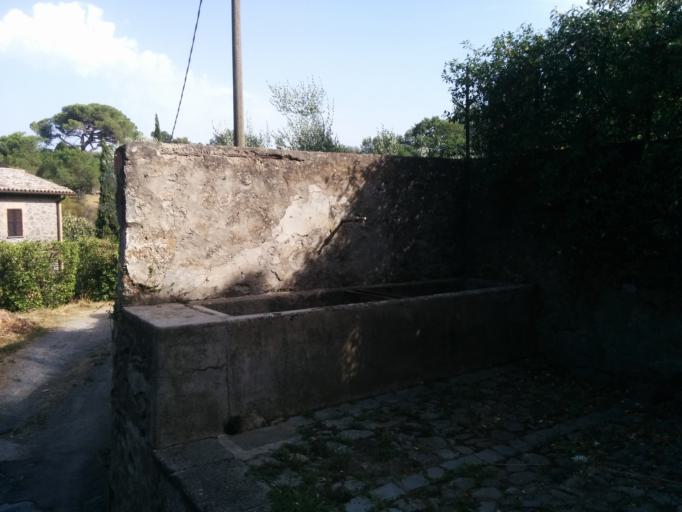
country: IT
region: Umbria
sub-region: Provincia di Terni
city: Sferracavallo
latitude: 42.7107
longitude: 12.0588
